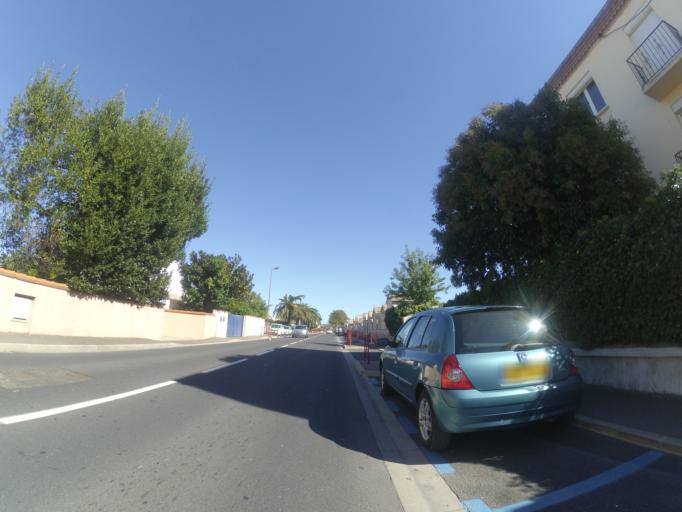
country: FR
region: Languedoc-Roussillon
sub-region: Departement des Pyrenees-Orientales
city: Saint-Esteve
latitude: 42.7092
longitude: 2.8486
